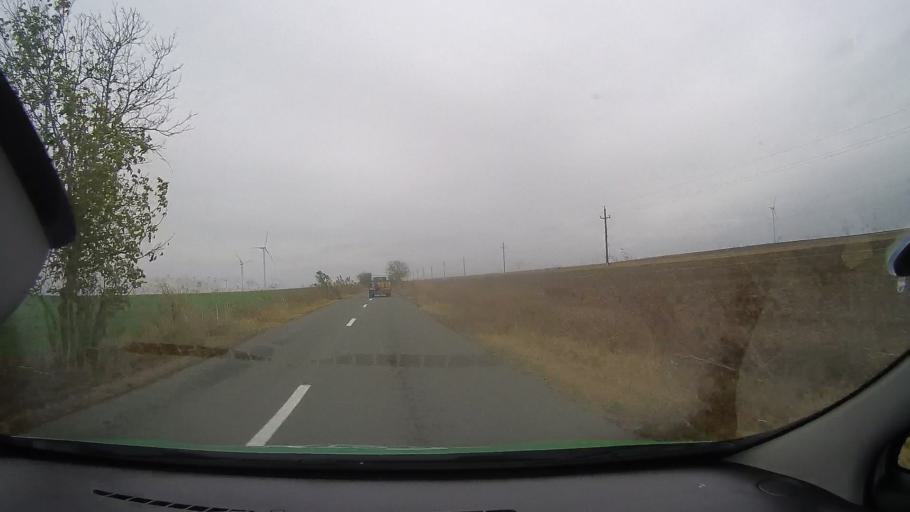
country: RO
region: Constanta
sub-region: Comuna Targusor
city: Targusor
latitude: 44.4738
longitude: 28.3831
